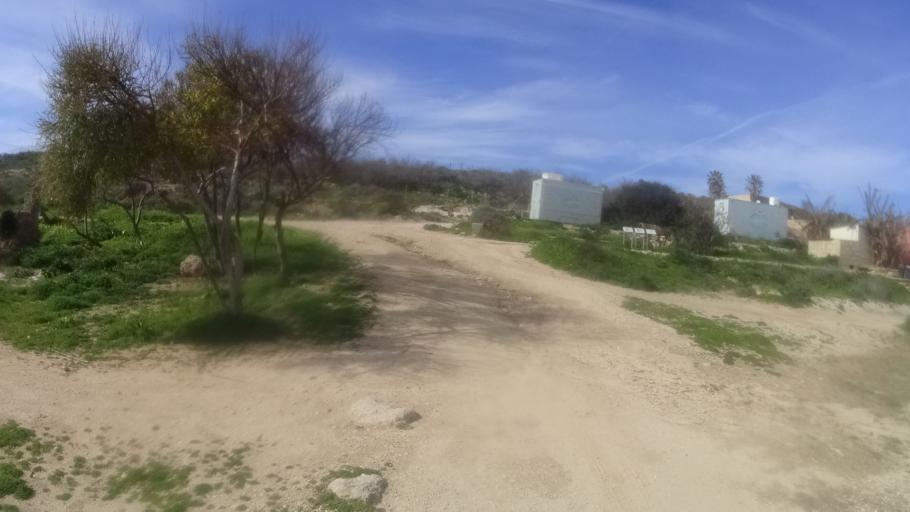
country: MT
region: Il-Qala
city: Qala
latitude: 36.0160
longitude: 14.3363
